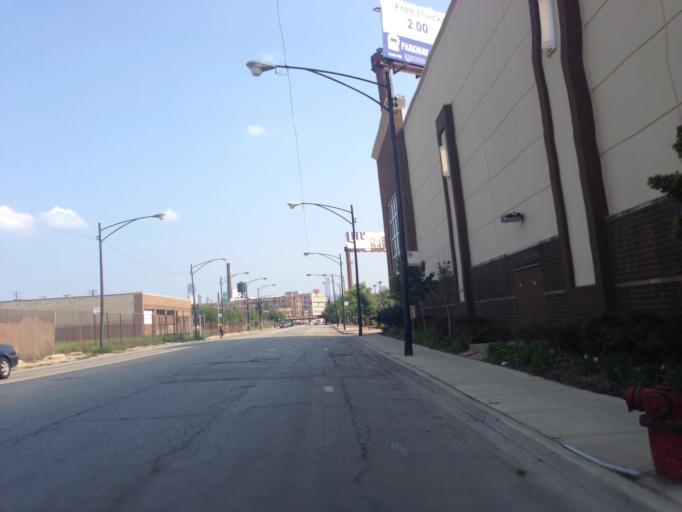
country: US
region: Illinois
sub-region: Cook County
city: Chicago
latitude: 41.9209
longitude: -87.6716
